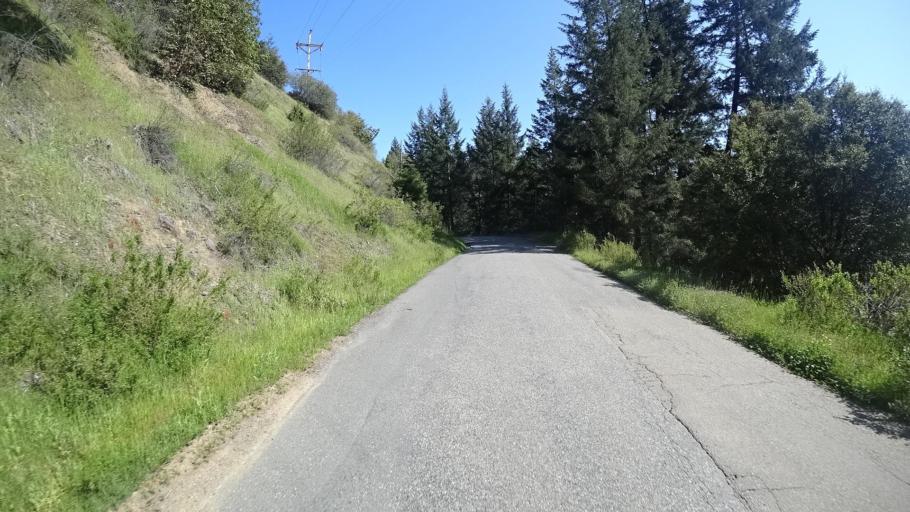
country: US
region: California
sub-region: Humboldt County
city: Redway
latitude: 40.0671
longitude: -123.6502
